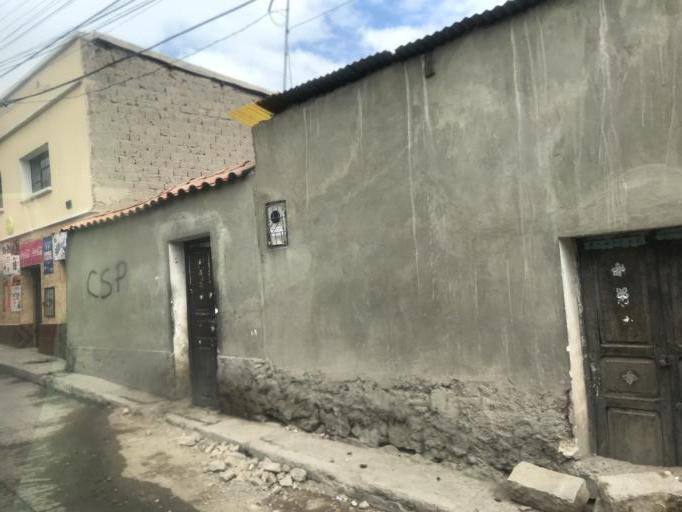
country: BO
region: Potosi
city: Potosi
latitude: -19.5977
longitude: -65.7487
